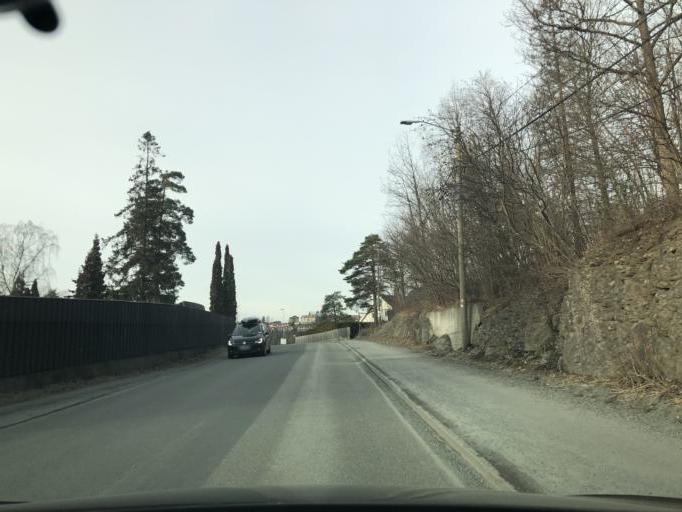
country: NO
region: Akershus
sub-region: Baerum
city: Sandvika
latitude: 59.8739
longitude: 10.5088
